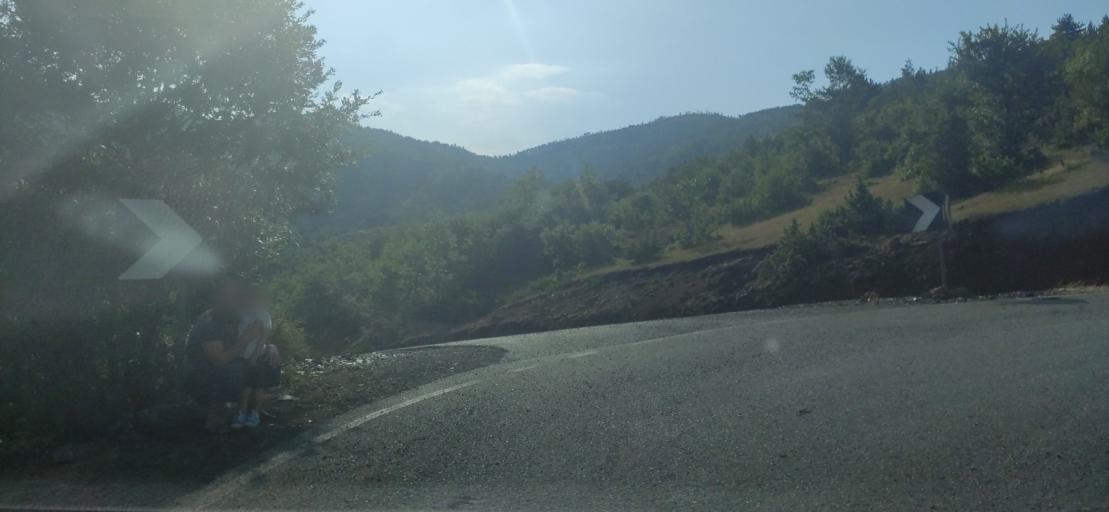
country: AL
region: Shkoder
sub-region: Rrethi i Pukes
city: Iballe
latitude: 42.1772
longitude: 20.0044
